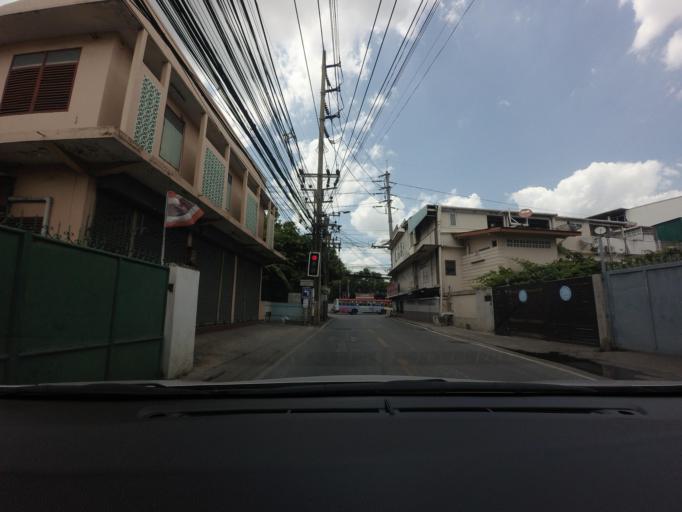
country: TH
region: Samut Prakan
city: Phra Samut Chedi
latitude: 13.6455
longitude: 100.5794
